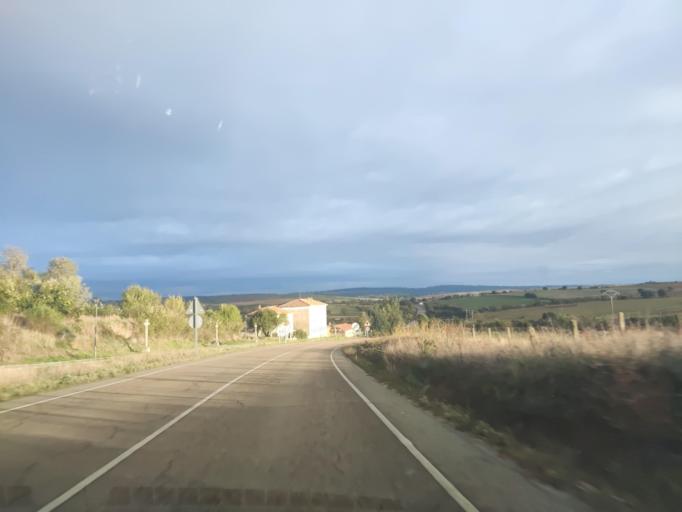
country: ES
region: Castille and Leon
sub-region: Provincia de Salamanca
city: San Felices de los Gallegos
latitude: 40.8484
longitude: -6.7037
